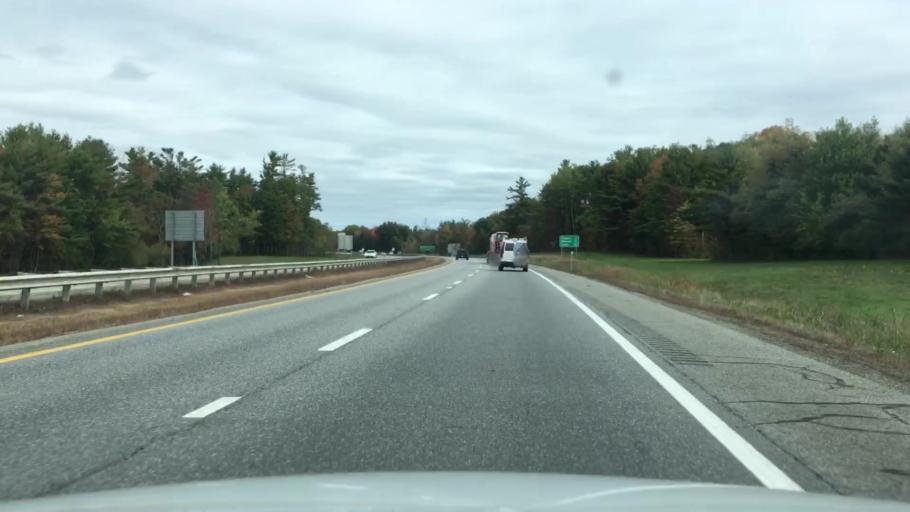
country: US
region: Maine
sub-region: Kennebec County
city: Gardiner
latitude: 44.2315
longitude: -69.8109
